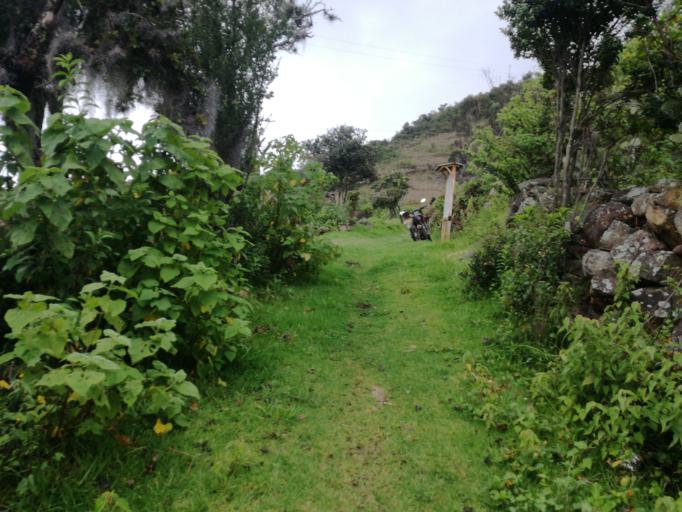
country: CO
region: Boyaca
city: Socha Viejo
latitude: 6.0052
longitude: -72.6812
